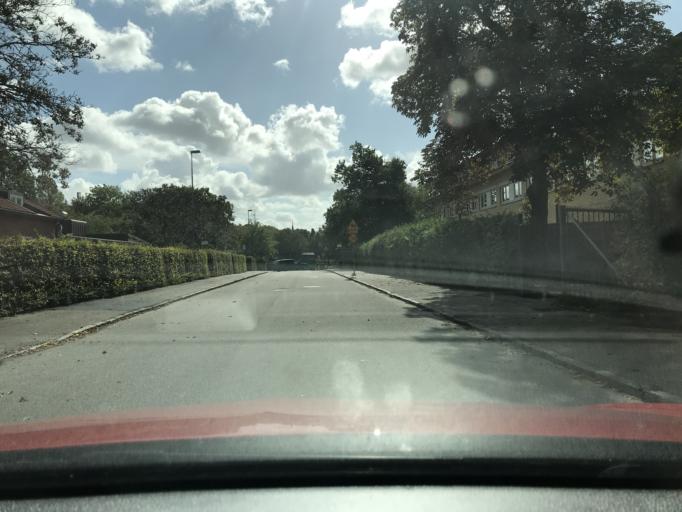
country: SE
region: Skane
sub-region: Lunds Kommun
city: Lund
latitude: 55.7182
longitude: 13.1949
